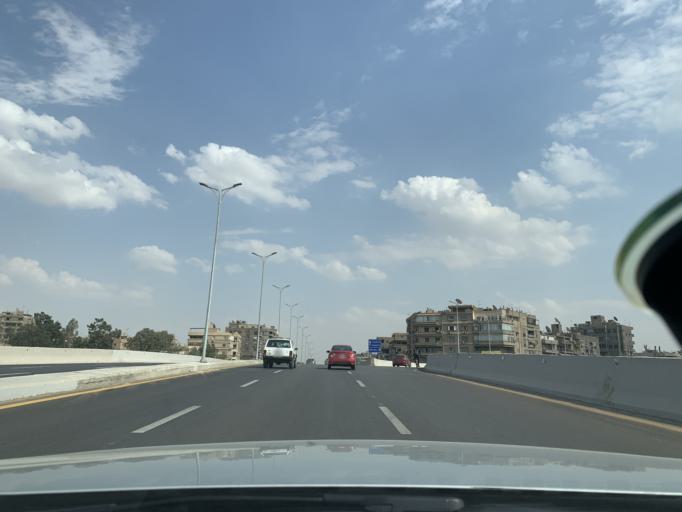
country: EG
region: Muhafazat al Qalyubiyah
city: Al Khankah
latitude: 30.1121
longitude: 31.3453
